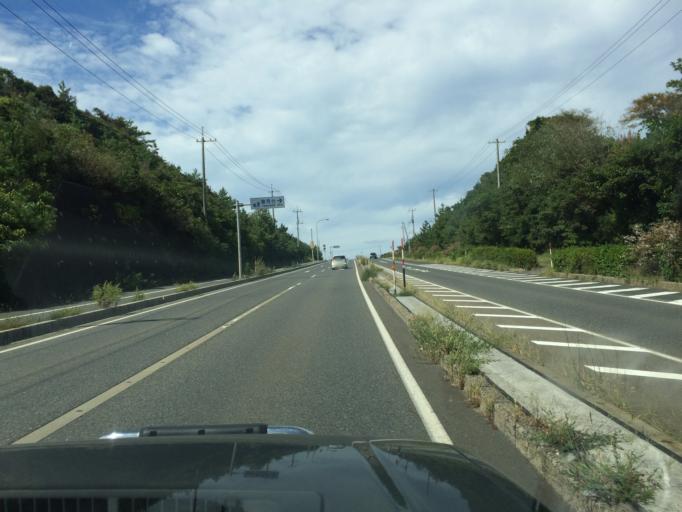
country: JP
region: Tottori
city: Tottori
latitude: 35.5175
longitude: 134.0656
